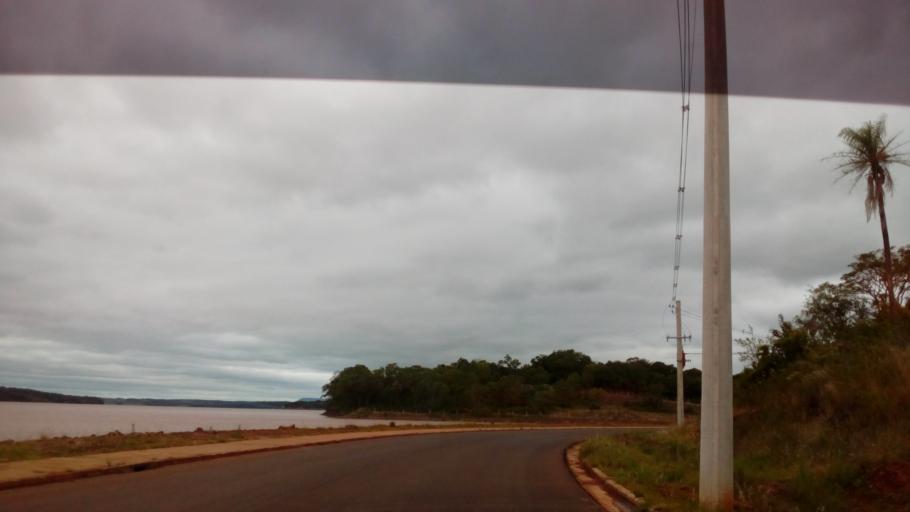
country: AR
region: Misiones
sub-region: Departamento de Candelaria
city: Candelaria
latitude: -27.4497
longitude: -55.7754
